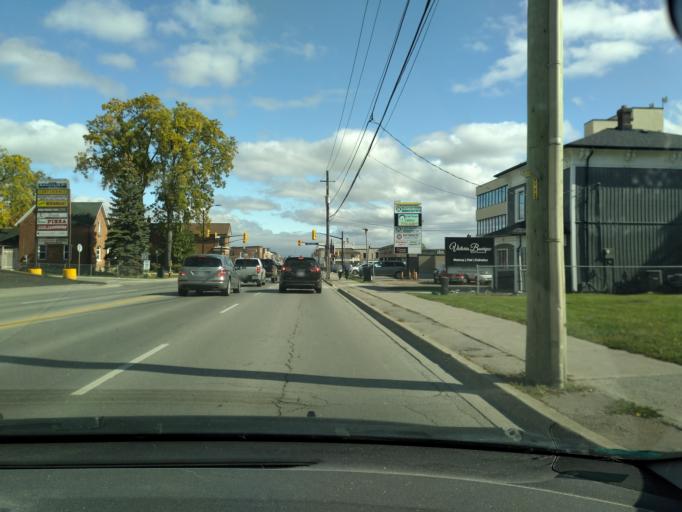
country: CA
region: Ontario
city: Bradford West Gwillimbury
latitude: 44.1135
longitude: -79.5683
